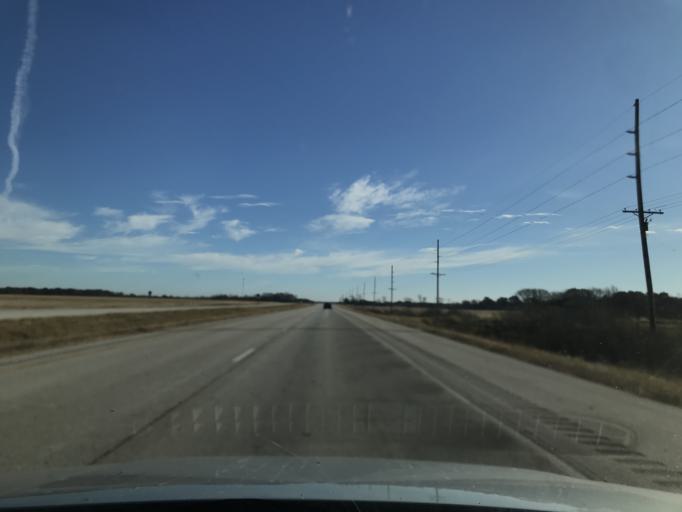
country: US
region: Illinois
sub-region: Hancock County
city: Carthage
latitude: 40.4150
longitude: -91.0527
